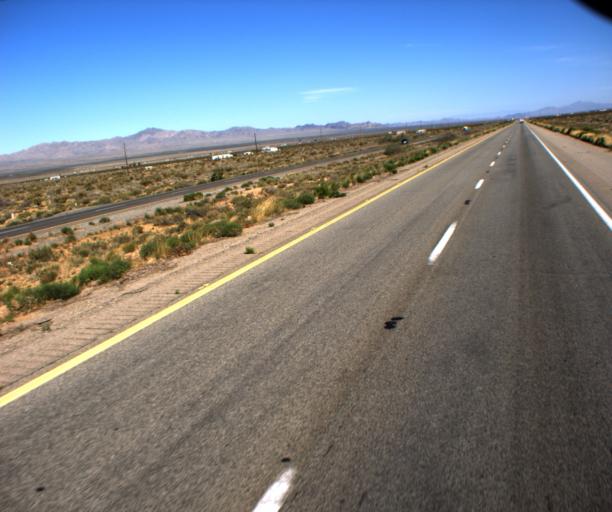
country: US
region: Arizona
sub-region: Mohave County
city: Dolan Springs
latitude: 35.4952
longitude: -114.3283
